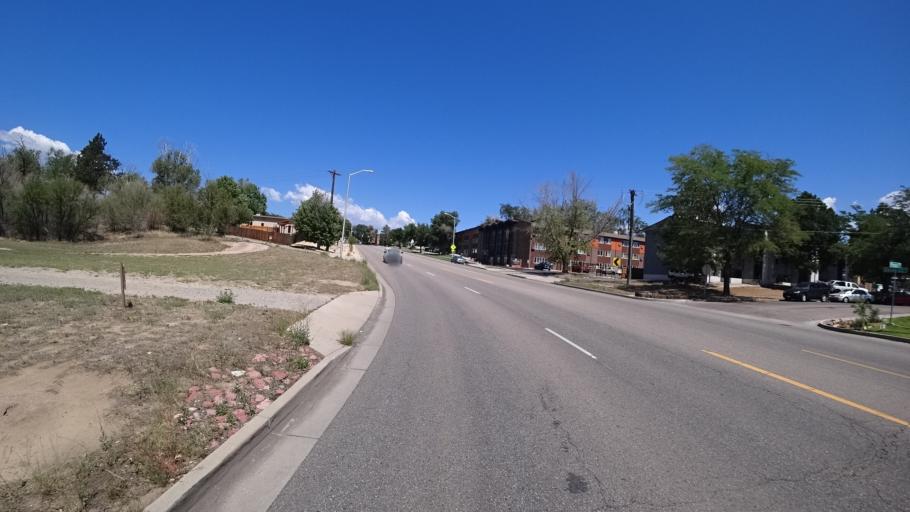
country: US
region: Colorado
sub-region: El Paso County
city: Colorado Springs
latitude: 38.8195
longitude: -104.7925
